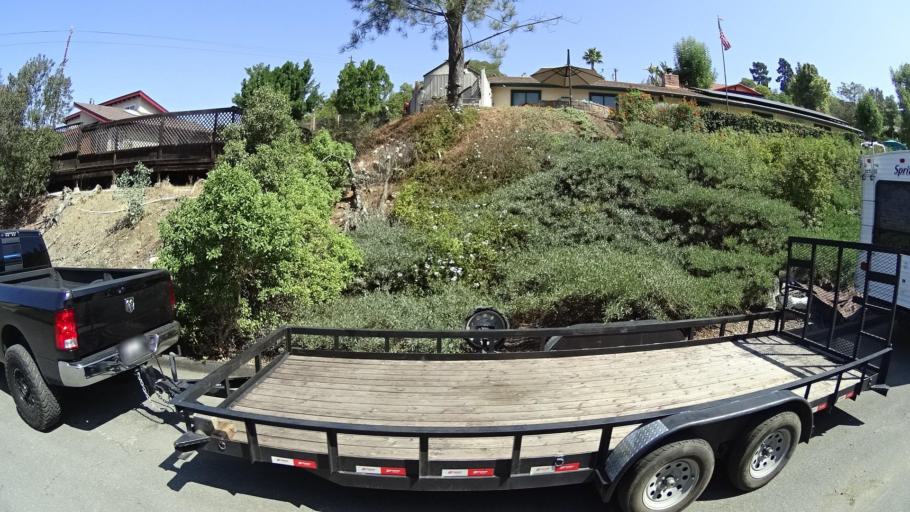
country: US
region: California
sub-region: San Diego County
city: Spring Valley
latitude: 32.7401
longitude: -116.9871
